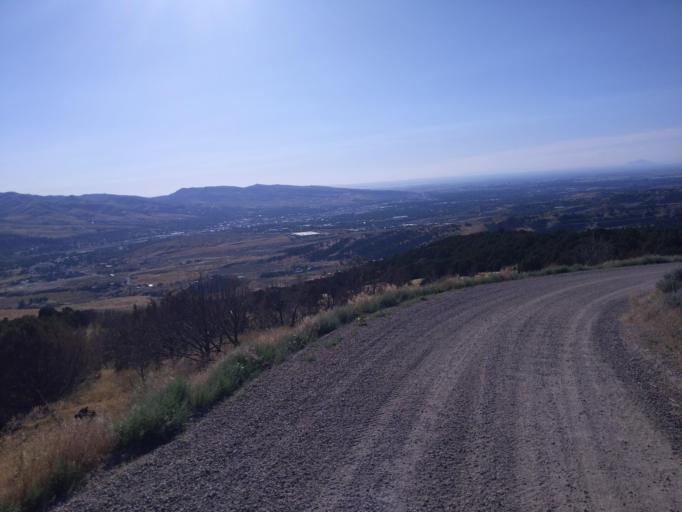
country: US
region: Idaho
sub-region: Bannock County
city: Pocatello
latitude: 42.8518
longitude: -112.3803
